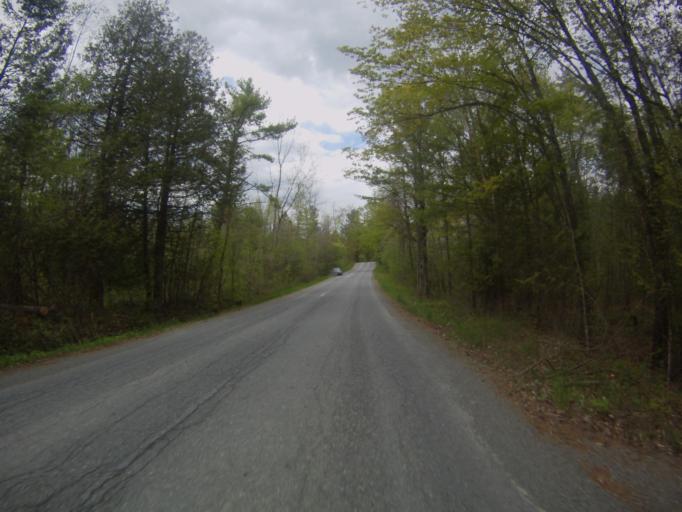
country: US
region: New York
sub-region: Essex County
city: Ticonderoga
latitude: 43.9293
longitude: -73.5056
